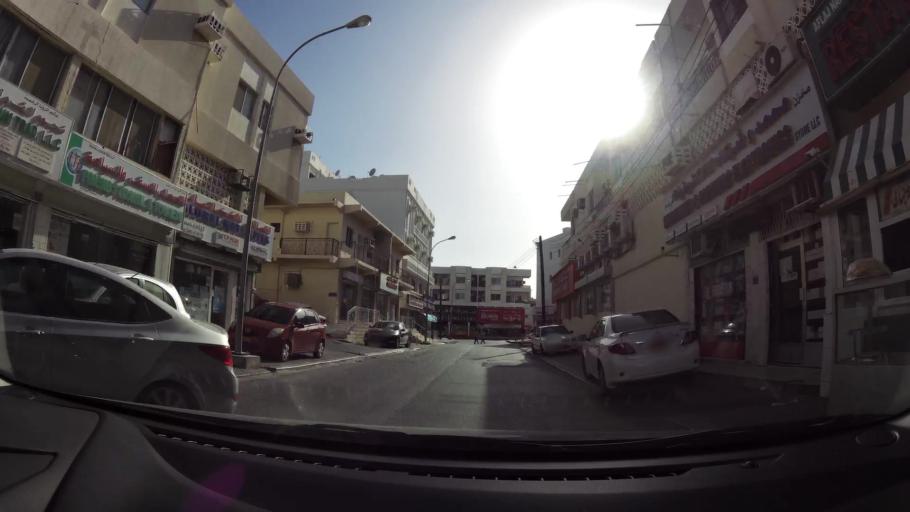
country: OM
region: Muhafazat Masqat
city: Muscat
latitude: 23.5887
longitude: 58.5466
